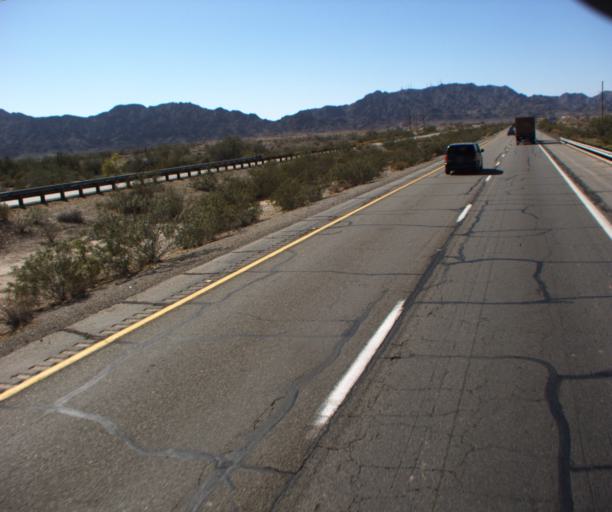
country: US
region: Arizona
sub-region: Yuma County
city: Wellton
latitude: 32.6647
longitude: -114.2735
